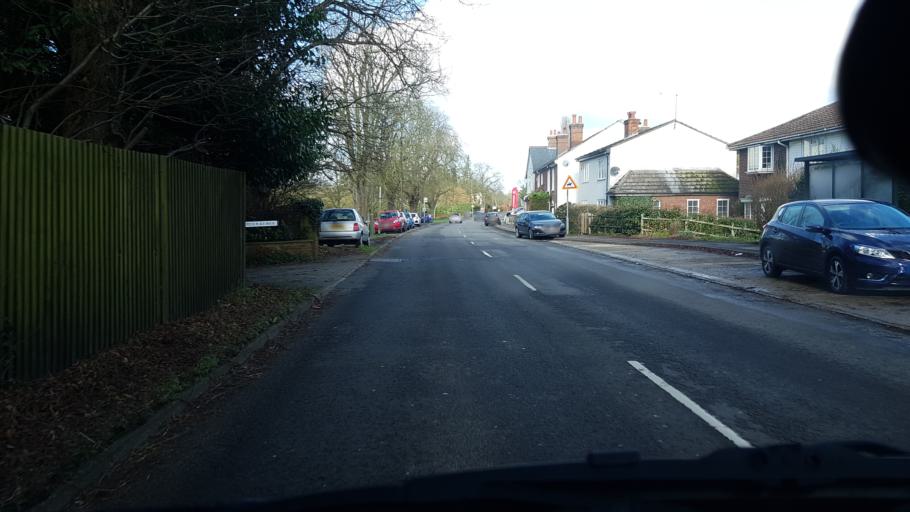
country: GB
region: England
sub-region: Surrey
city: Guildford
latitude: 51.2634
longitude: -0.5970
